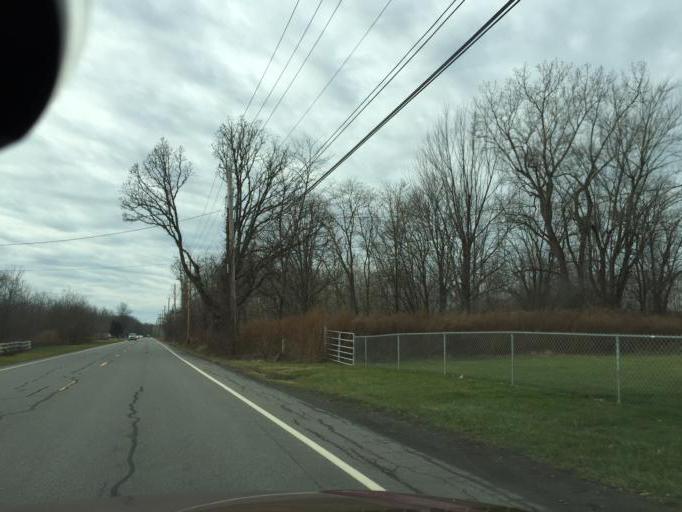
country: US
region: New York
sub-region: Monroe County
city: Scottsville
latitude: 43.0910
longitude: -77.7134
